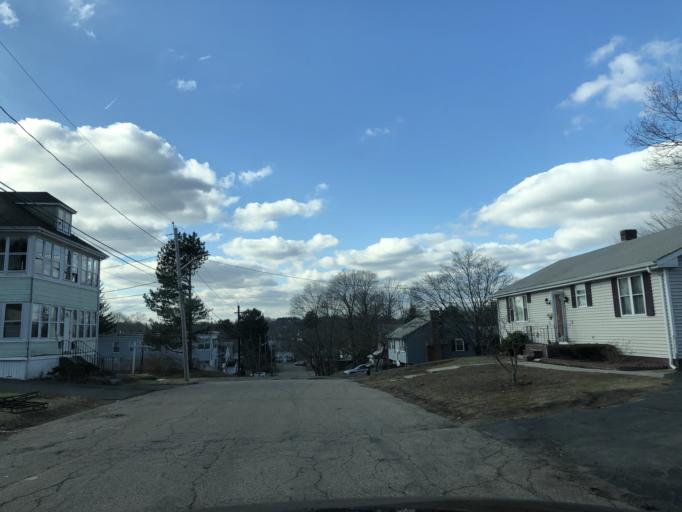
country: US
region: Massachusetts
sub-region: Plymouth County
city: Brockton
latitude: 42.1091
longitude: -71.0162
